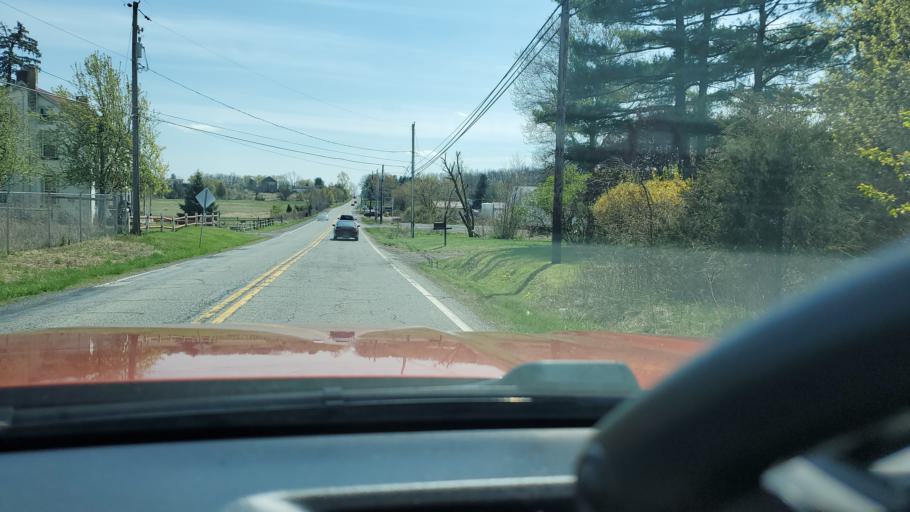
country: US
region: Pennsylvania
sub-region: Montgomery County
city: Red Hill
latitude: 40.3634
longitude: -75.4826
